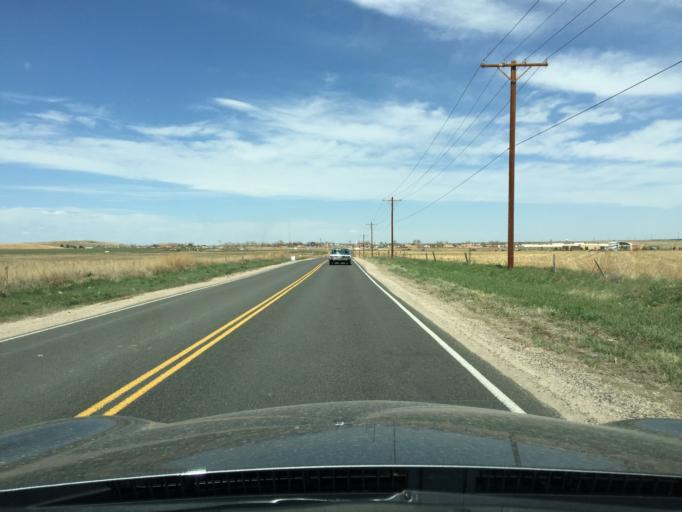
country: US
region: Colorado
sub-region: Boulder County
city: Erie
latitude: 39.9939
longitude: -104.9972
